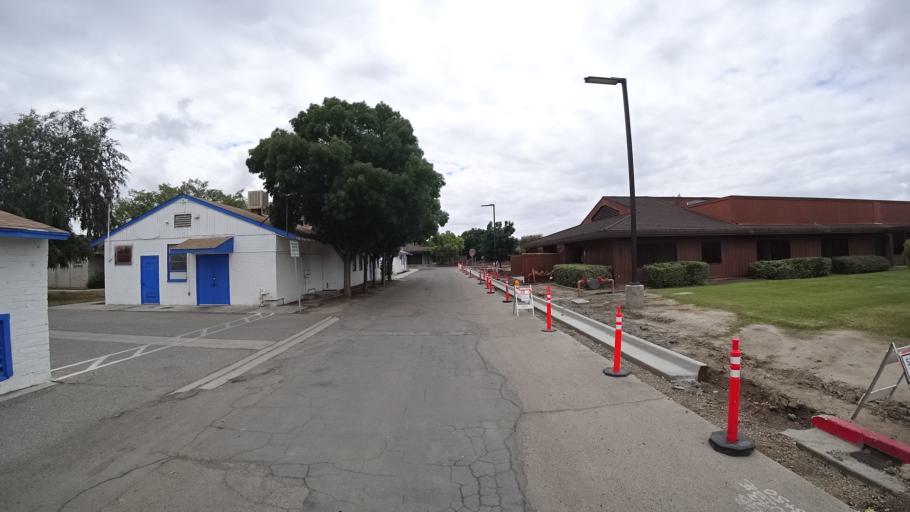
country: US
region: California
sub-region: Kings County
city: Hanford
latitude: 36.3315
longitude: -119.6669
